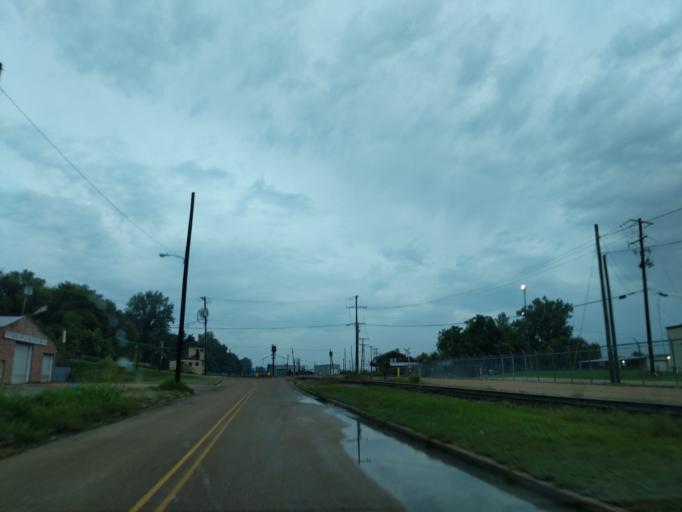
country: US
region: Mississippi
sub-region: Warren County
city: Vicksburg
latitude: 32.3467
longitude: -90.8862
